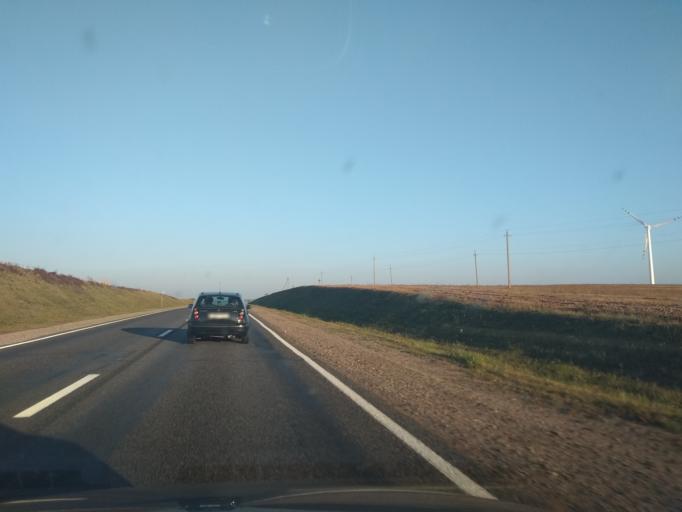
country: BY
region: Grodnenskaya
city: Zel'va
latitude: 53.1419
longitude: 24.7874
